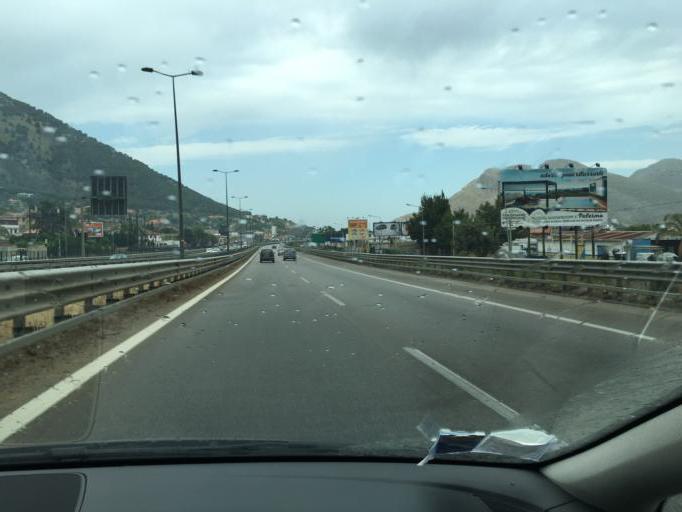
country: IT
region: Sicily
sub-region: Palermo
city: Palermo
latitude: 38.1719
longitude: 13.2988
